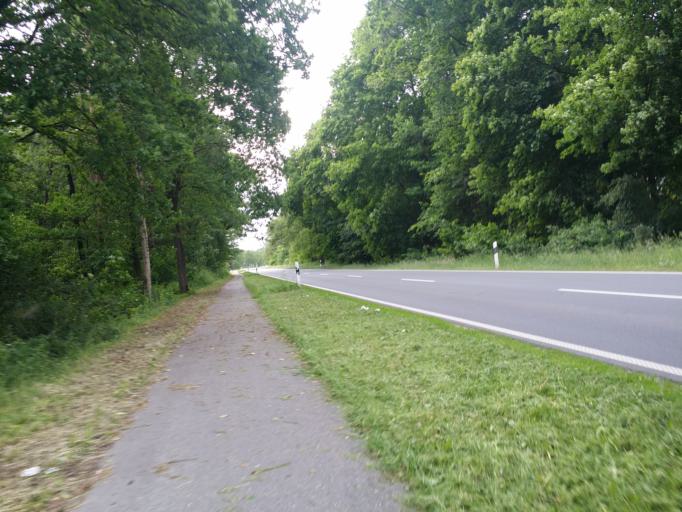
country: DE
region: Lower Saxony
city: Friedeburg
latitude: 53.4172
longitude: 7.8831
